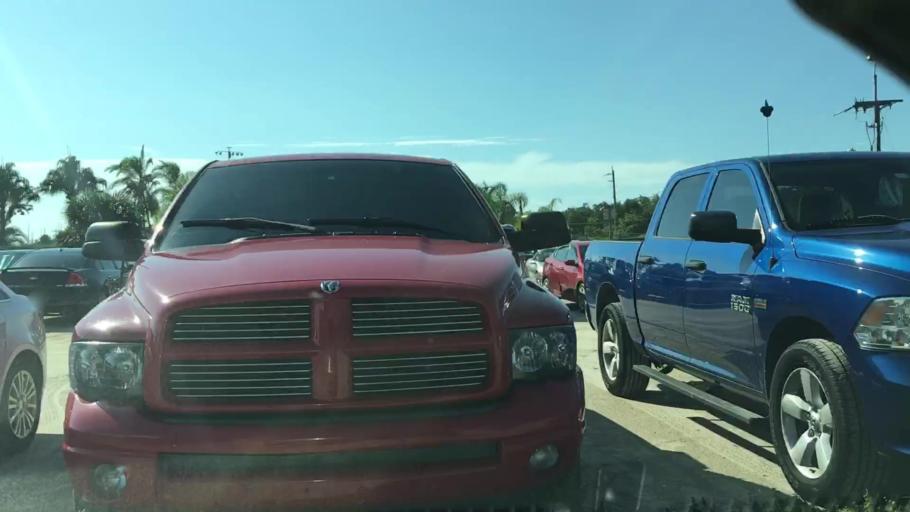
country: US
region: Florida
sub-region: Brevard County
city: Titusville
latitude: 28.6232
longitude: -80.8140
